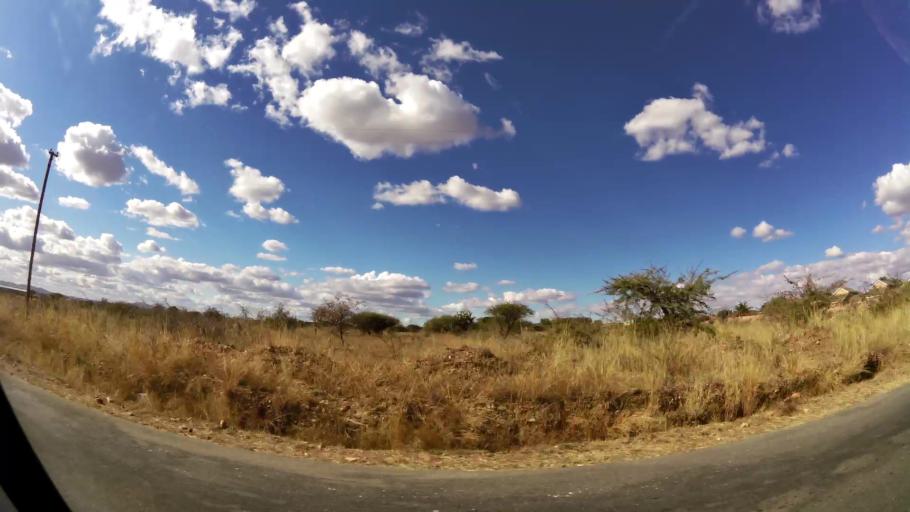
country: ZA
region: Limpopo
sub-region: Capricorn District Municipality
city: Polokwane
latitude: -23.8788
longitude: 29.4813
